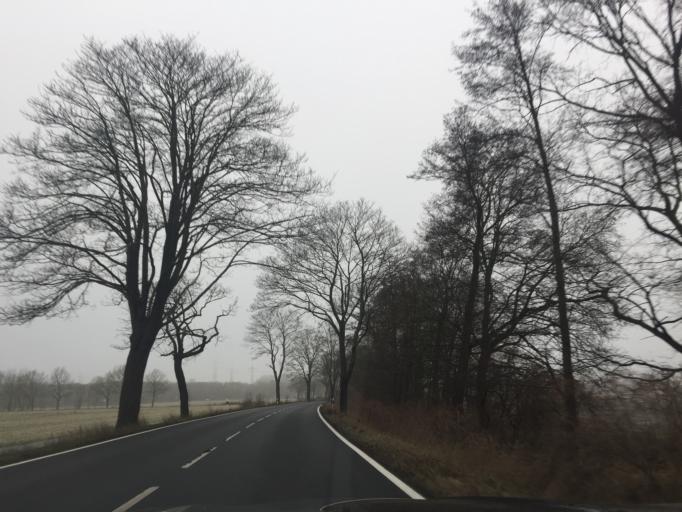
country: DE
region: Brandenburg
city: Velten
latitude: 52.6641
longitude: 13.1648
